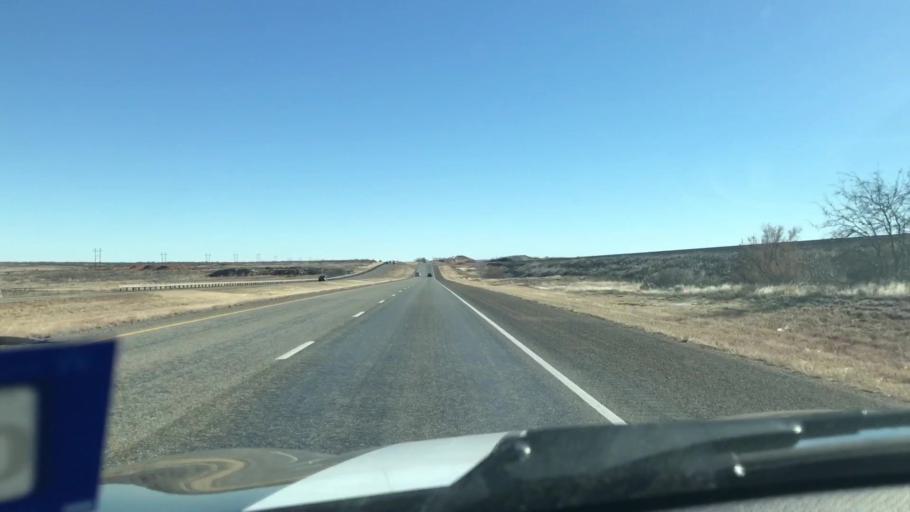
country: US
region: Texas
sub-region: Garza County
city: Post
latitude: 33.1134
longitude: -101.2744
